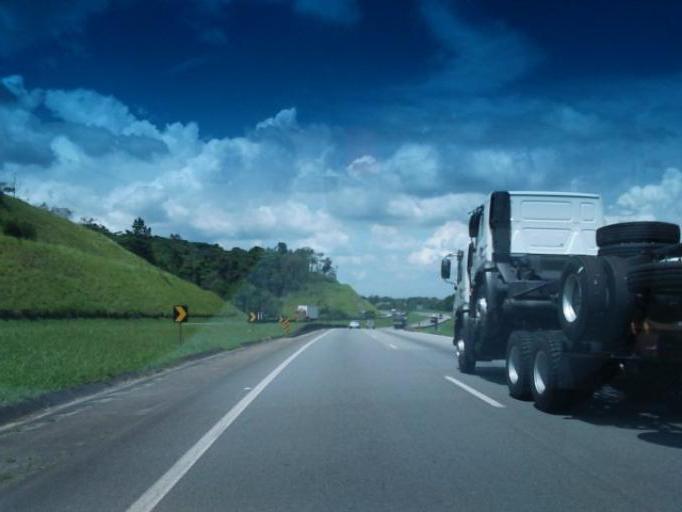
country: BR
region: Sao Paulo
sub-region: Juquitiba
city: Juquitiba
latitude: -23.9743
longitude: -47.1390
